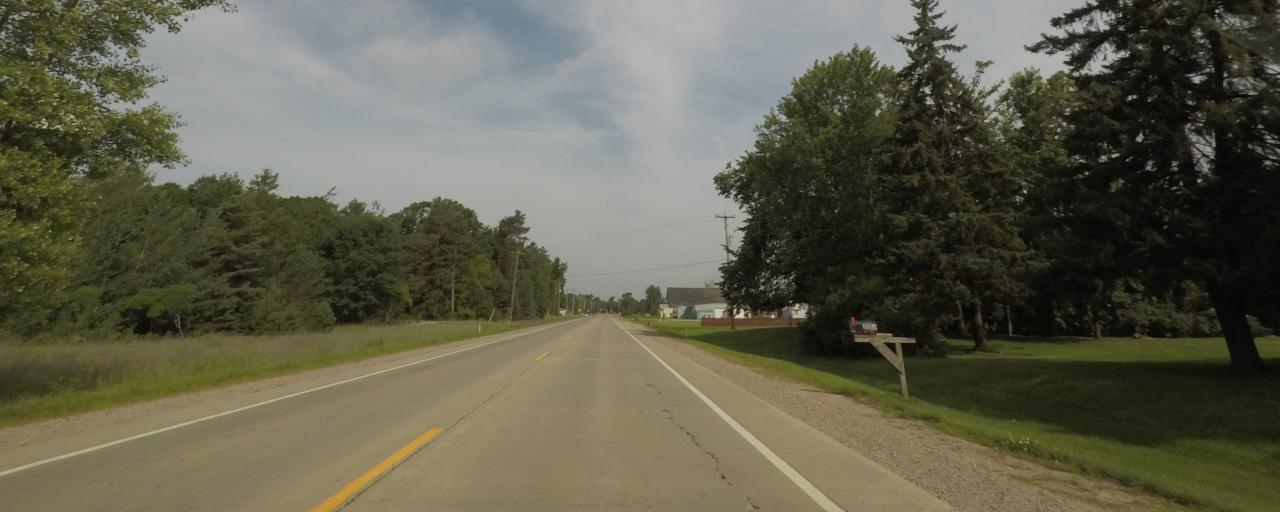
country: US
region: Wisconsin
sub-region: Portage County
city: Plover
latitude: 44.4424
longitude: -89.5357
